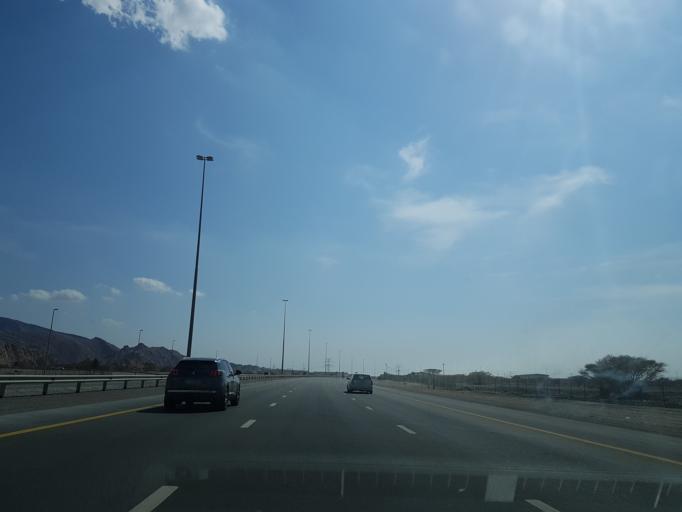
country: AE
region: Ra's al Khaymah
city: Ras al-Khaimah
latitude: 25.7832
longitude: 56.0313
